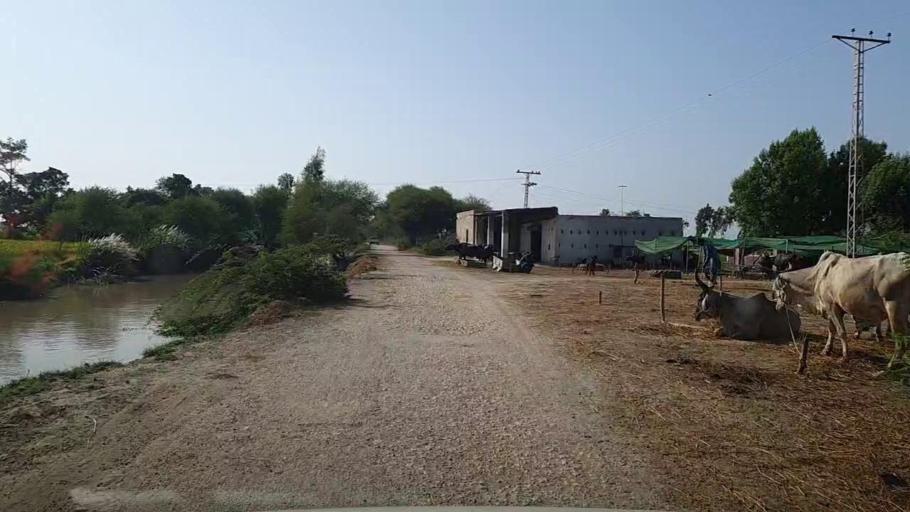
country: PK
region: Sindh
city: Kario
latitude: 24.8051
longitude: 68.5476
